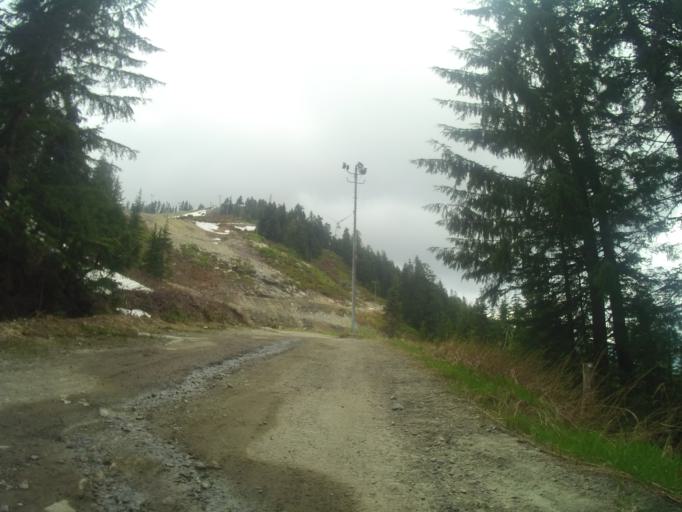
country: CA
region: British Columbia
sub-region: Fraser Valley Regional District
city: North Vancouver
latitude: 49.3813
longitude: -123.0757
